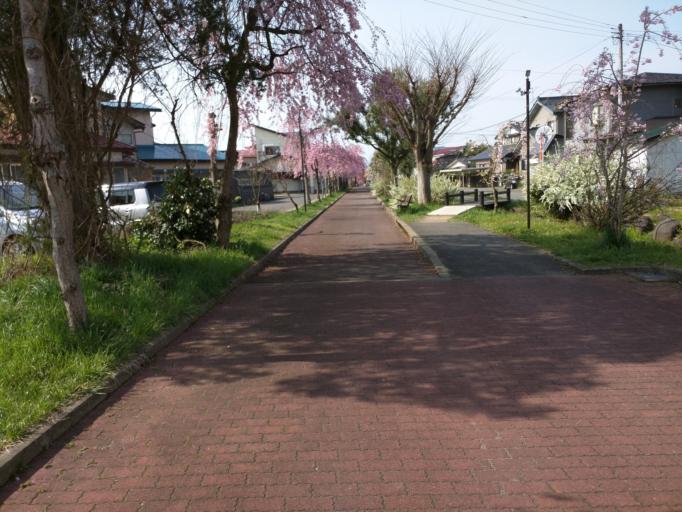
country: JP
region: Fukushima
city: Kitakata
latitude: 37.6520
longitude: 139.8646
